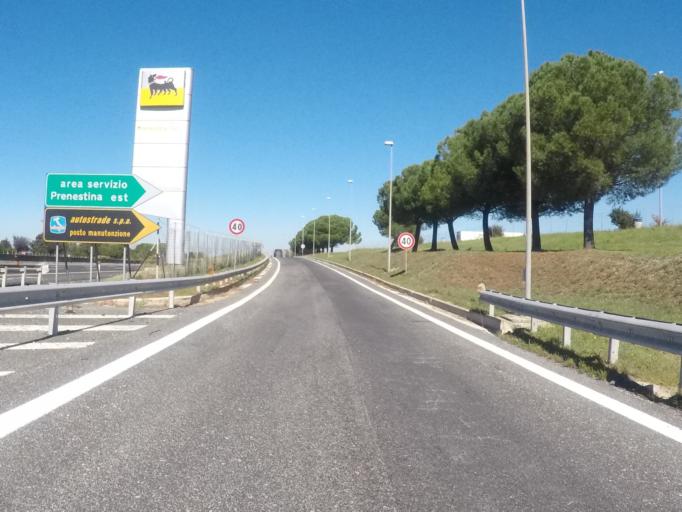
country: IT
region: Latium
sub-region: Citta metropolitana di Roma Capitale
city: Valle Martella
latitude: 41.8883
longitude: 12.7609
